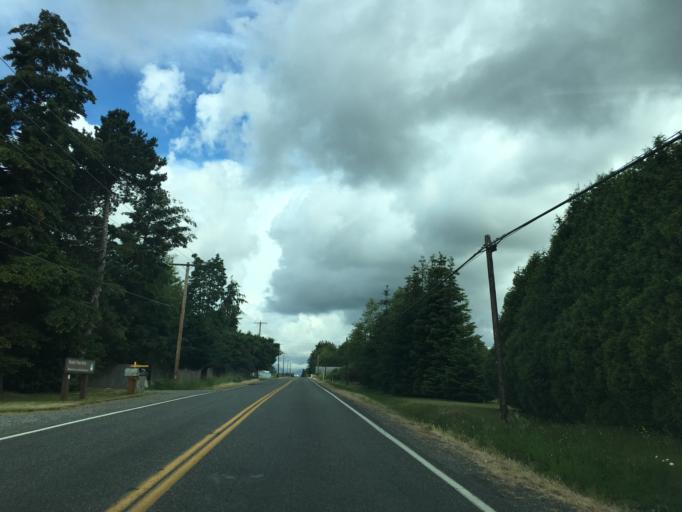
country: US
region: Washington
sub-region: Whatcom County
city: Birch Bay
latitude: 48.9311
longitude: -122.7263
